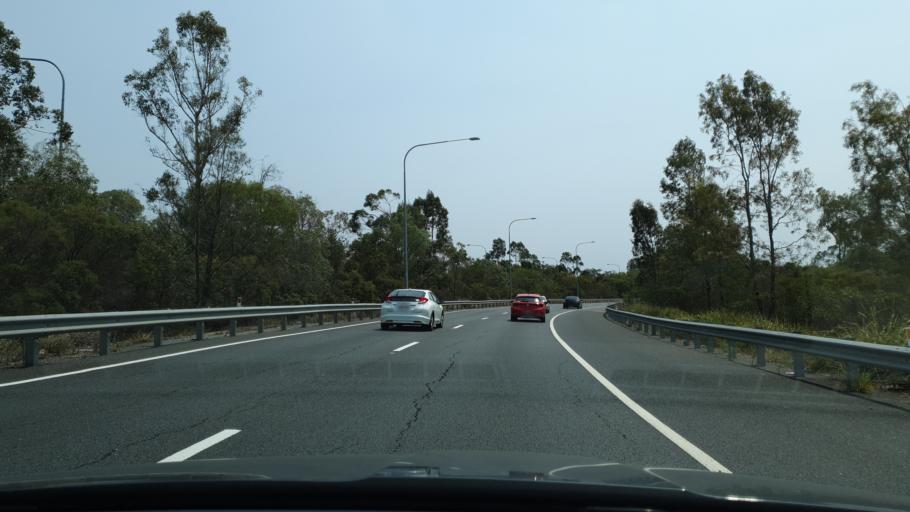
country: AU
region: Queensland
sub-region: Brisbane
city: Wacol
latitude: -27.5791
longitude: 152.9439
